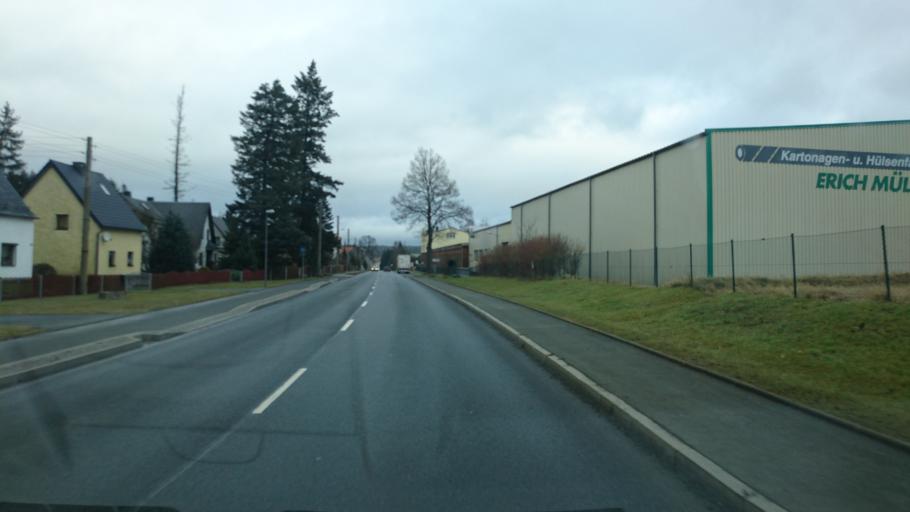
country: DE
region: Saxony
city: Muhltroff
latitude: 50.5360
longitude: 11.9177
